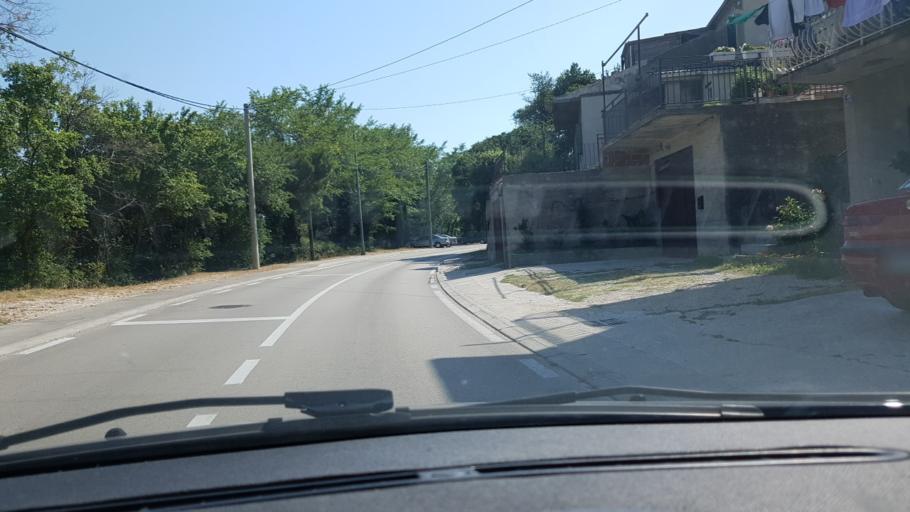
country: HR
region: Splitsko-Dalmatinska
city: Klis
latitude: 43.5663
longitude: 16.5284
